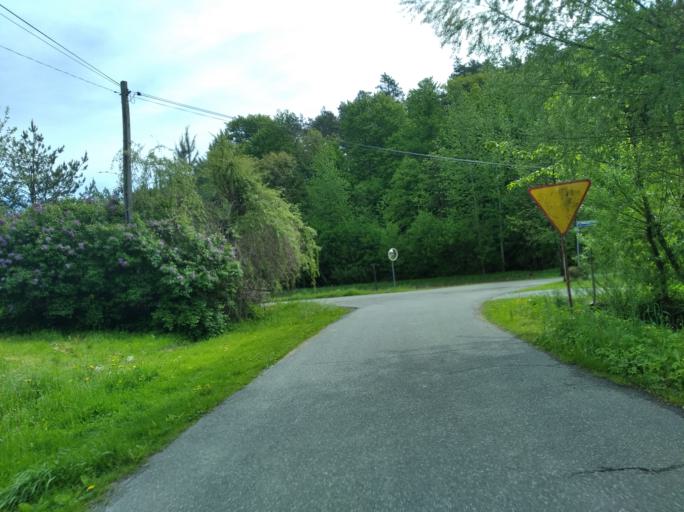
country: PL
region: Subcarpathian Voivodeship
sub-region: Powiat strzyzowski
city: Strzyzow
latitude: 49.9260
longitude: 21.7532
